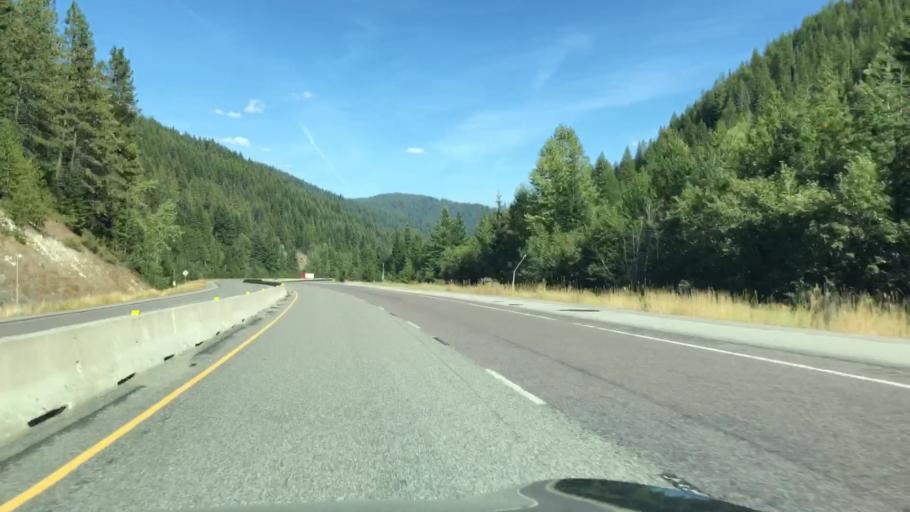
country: US
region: Montana
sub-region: Sanders County
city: Thompson Falls
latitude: 47.4171
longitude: -115.5620
